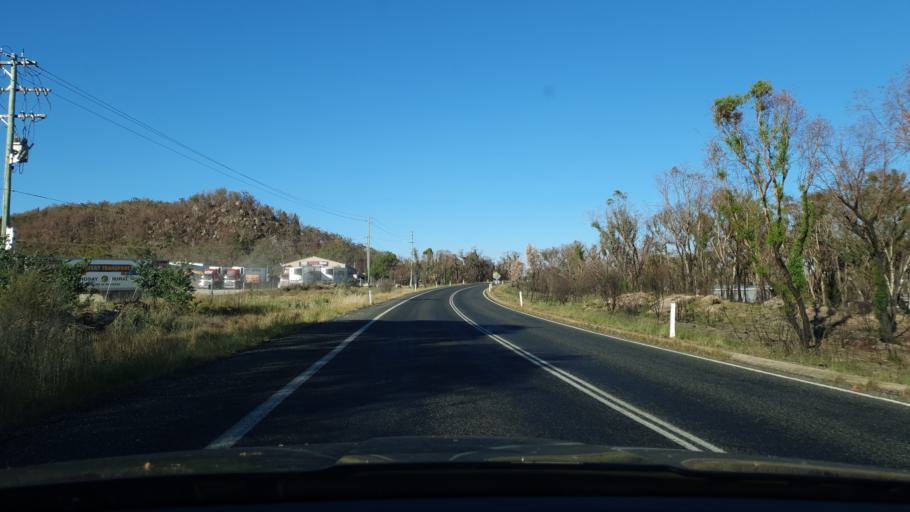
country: AU
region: Queensland
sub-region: Southern Downs
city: Stanthorpe
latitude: -28.6526
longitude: 151.9189
